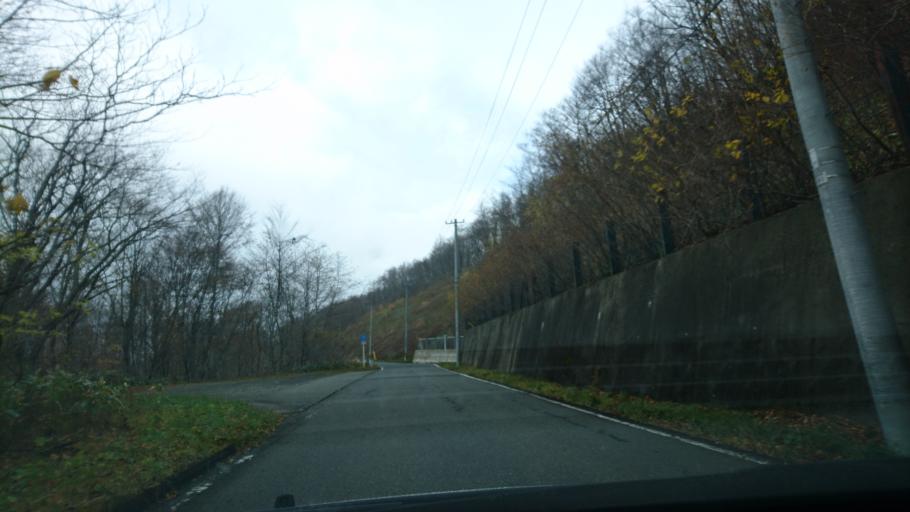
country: JP
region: Iwate
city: Ichinoseki
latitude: 38.9197
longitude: 140.8447
